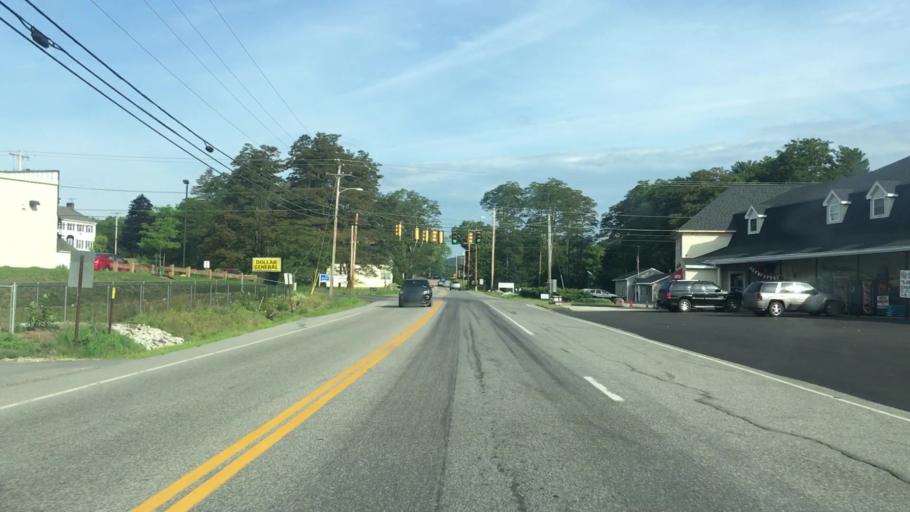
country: US
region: Maine
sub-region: York County
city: Limington
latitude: 43.7467
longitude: -70.6785
